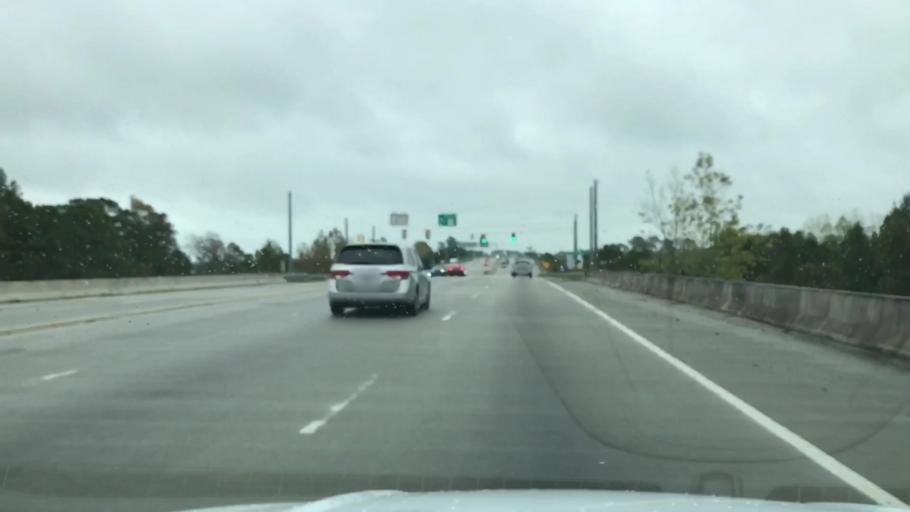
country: US
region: South Carolina
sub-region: Horry County
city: Myrtle Beach
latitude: 33.7542
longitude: -78.8528
